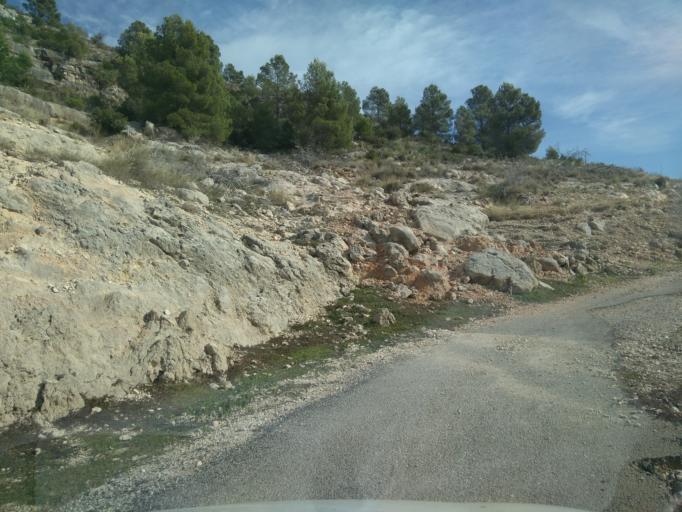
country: ES
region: Valencia
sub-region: Provincia de Valencia
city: Sumacarcer
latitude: 39.1540
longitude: -0.6571
